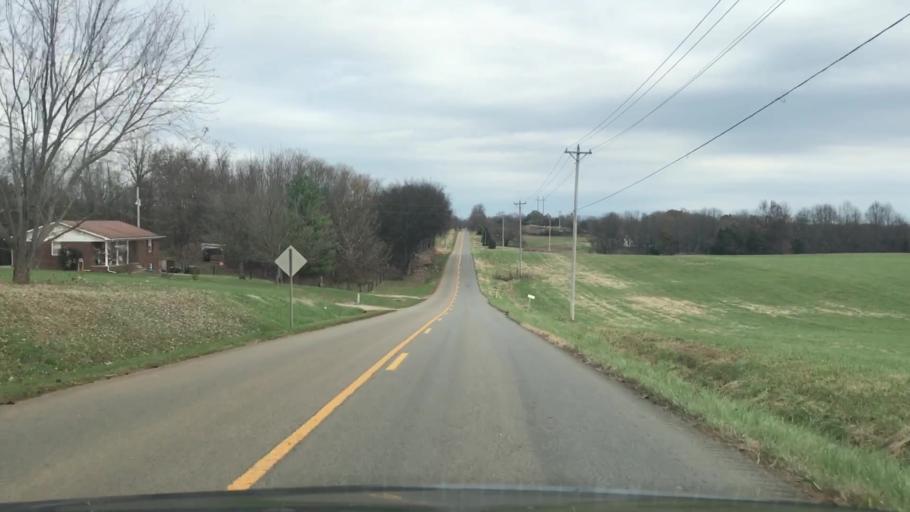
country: US
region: Kentucky
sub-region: Metcalfe County
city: Edmonton
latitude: 36.8969
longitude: -85.6587
